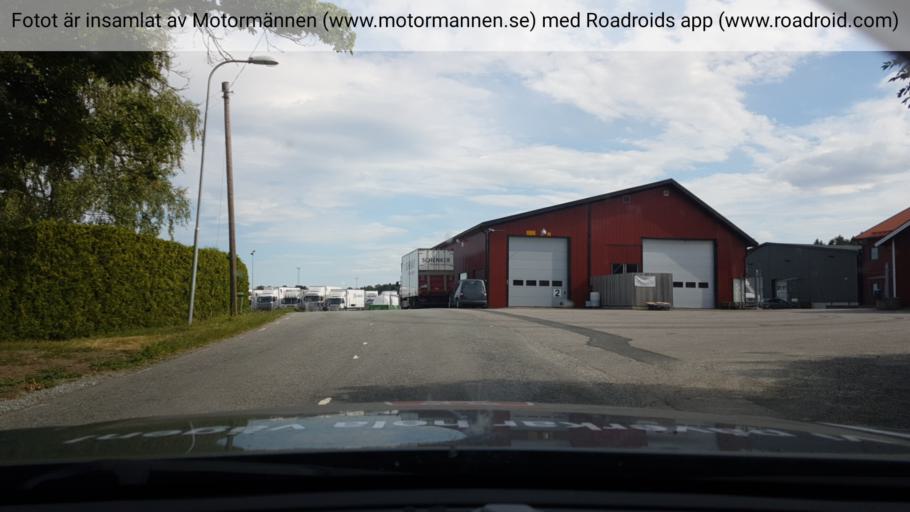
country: SE
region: Uppsala
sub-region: Enkopings Kommun
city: Grillby
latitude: 59.6579
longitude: 17.2457
